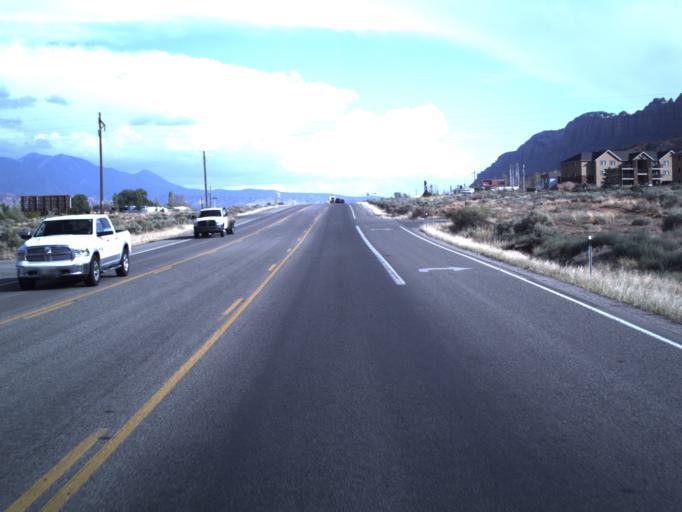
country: US
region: Utah
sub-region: Grand County
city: Moab
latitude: 38.5262
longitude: -109.5014
